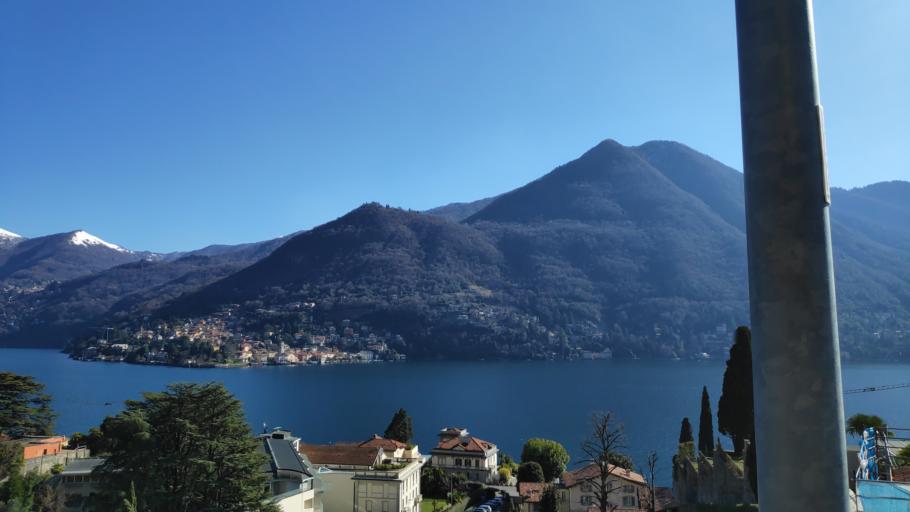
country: IT
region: Lombardy
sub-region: Provincia di Como
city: Moltrasio
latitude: 45.8610
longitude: 9.0993
